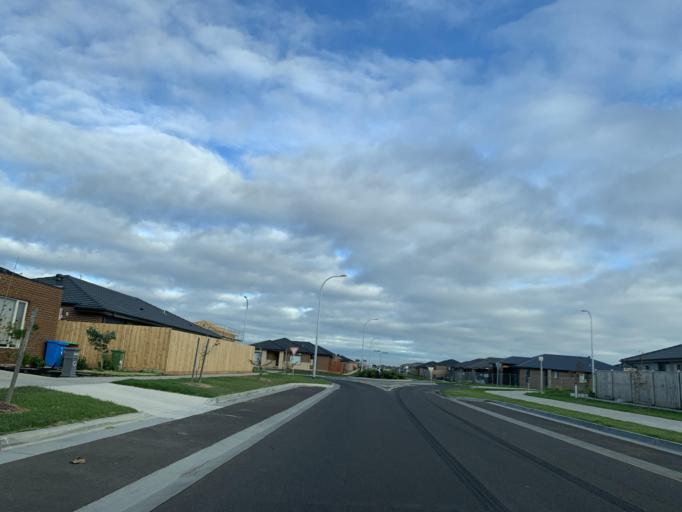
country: AU
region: Victoria
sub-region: Casey
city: Junction Village
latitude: -38.1301
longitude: 145.3164
